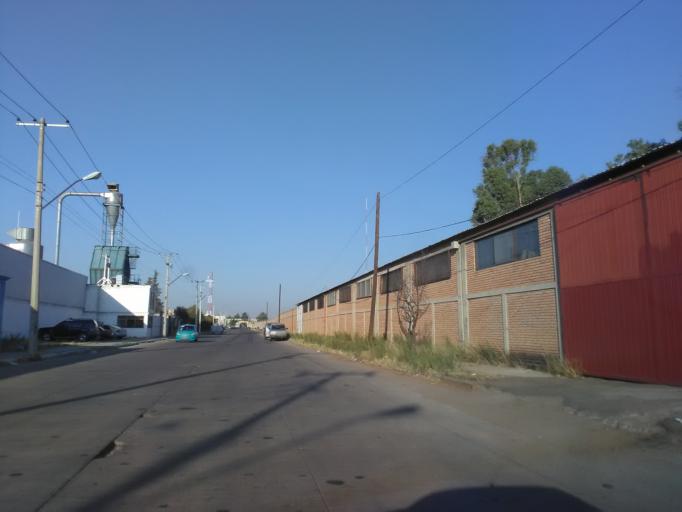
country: MX
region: Durango
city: Victoria de Durango
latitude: 24.0635
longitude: -104.6112
